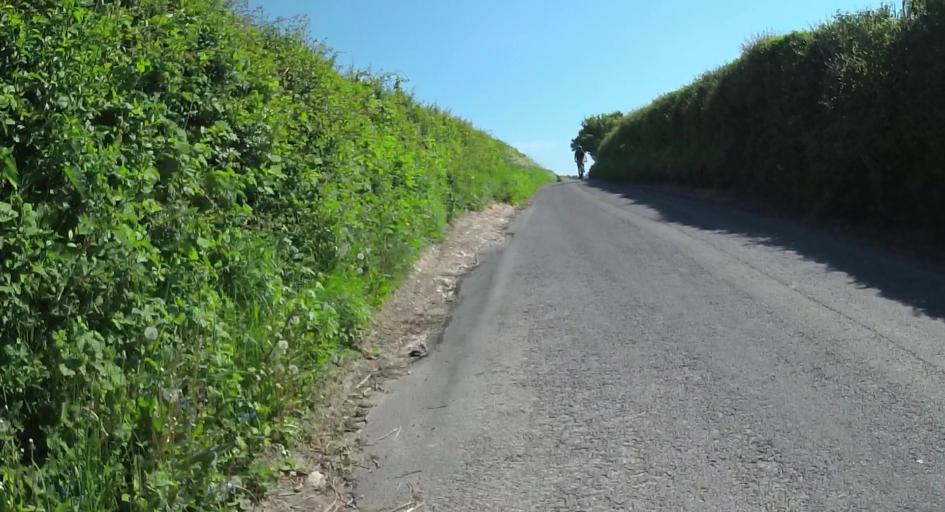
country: GB
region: England
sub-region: Hampshire
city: Kings Worthy
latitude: 51.0778
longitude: -1.2702
